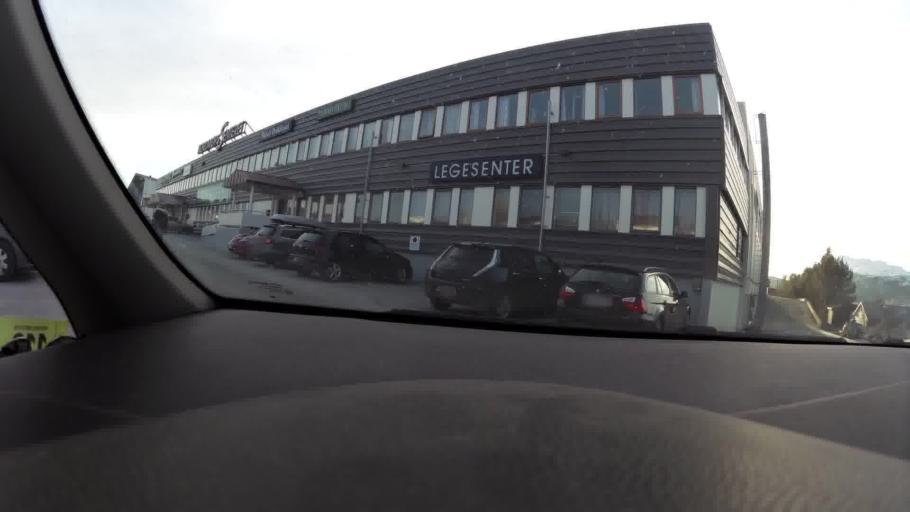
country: NO
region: More og Romsdal
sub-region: Kristiansund
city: Rensvik
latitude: 63.0866
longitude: 7.8826
